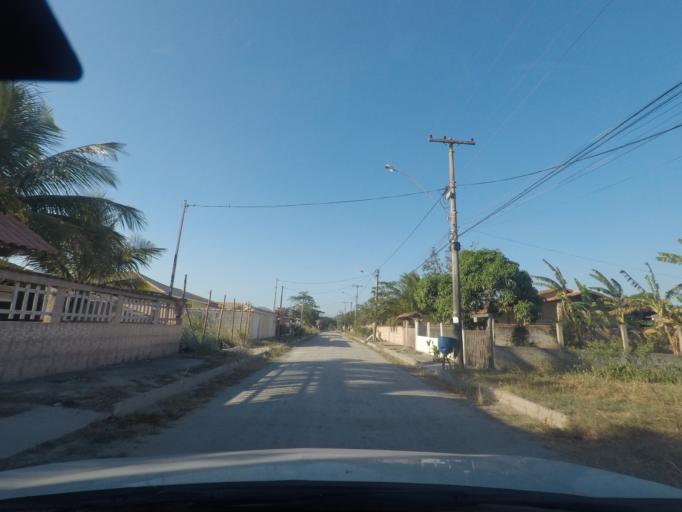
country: BR
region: Rio de Janeiro
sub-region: Marica
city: Marica
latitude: -22.9610
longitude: -42.9370
